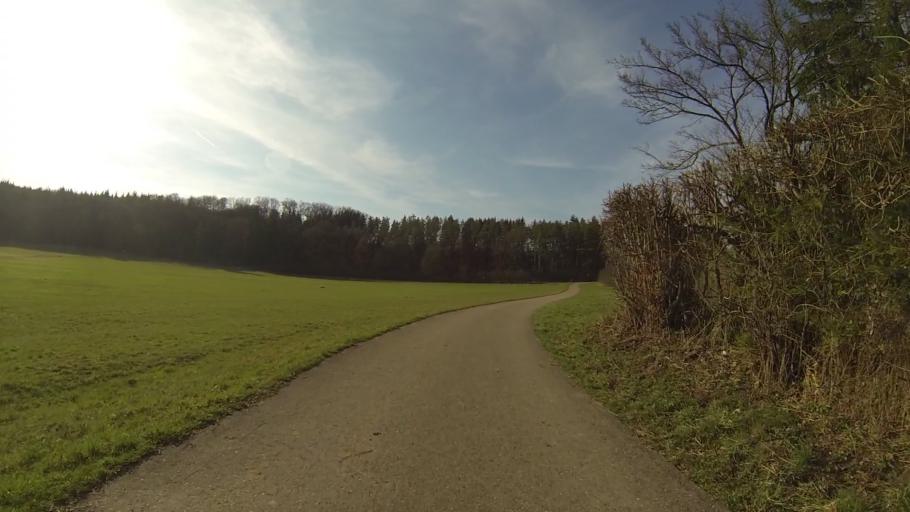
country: DE
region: Baden-Wuerttemberg
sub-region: Regierungsbezirk Stuttgart
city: Hermaringen
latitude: 48.5875
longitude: 10.2223
